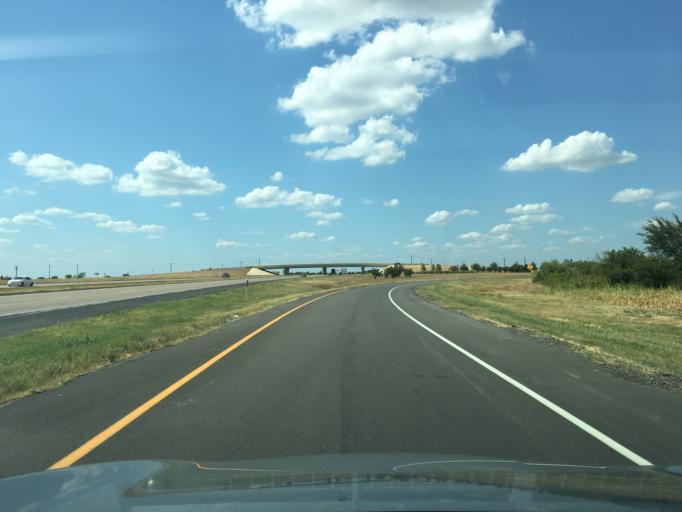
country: US
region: Texas
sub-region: Tarrant County
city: Mansfield
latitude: 32.5340
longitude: -97.1008
